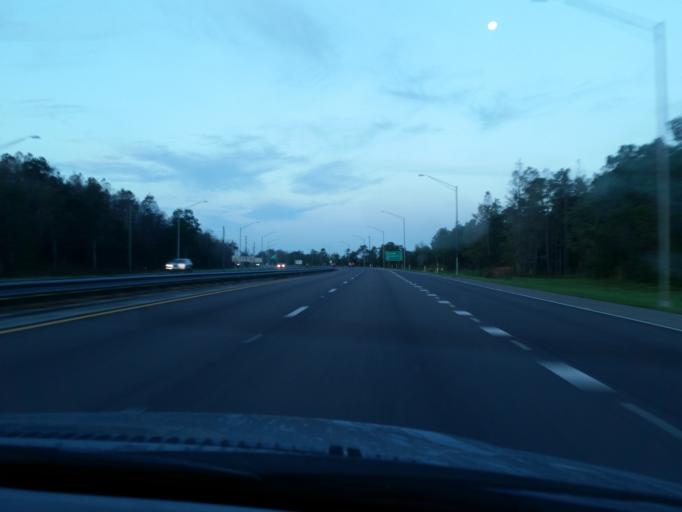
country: US
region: Florida
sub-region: Orange County
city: Conway
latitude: 28.4514
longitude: -81.2444
